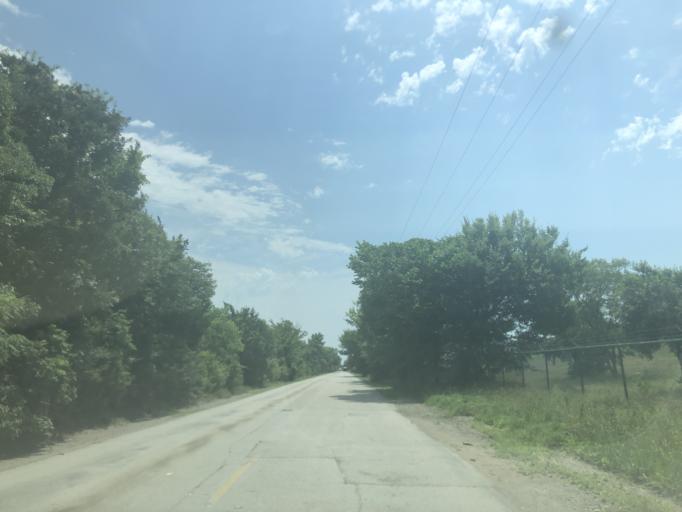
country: US
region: Texas
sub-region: Dallas County
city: Irving
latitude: 32.7866
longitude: -96.9482
